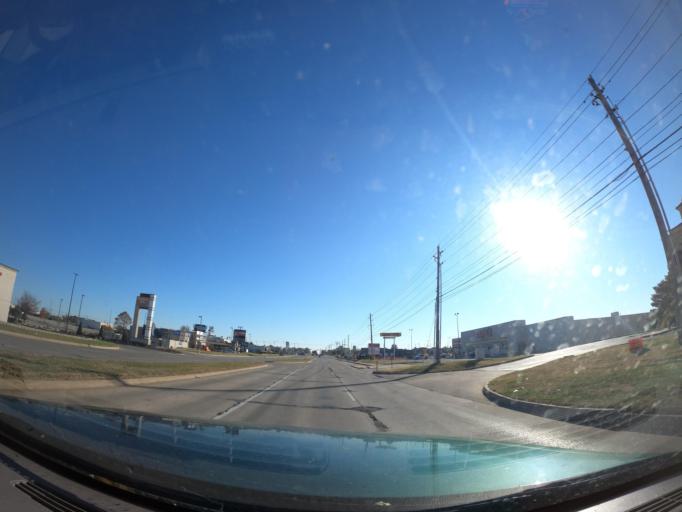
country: US
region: Oklahoma
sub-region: Tulsa County
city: Jenks
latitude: 36.0639
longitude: -95.8865
